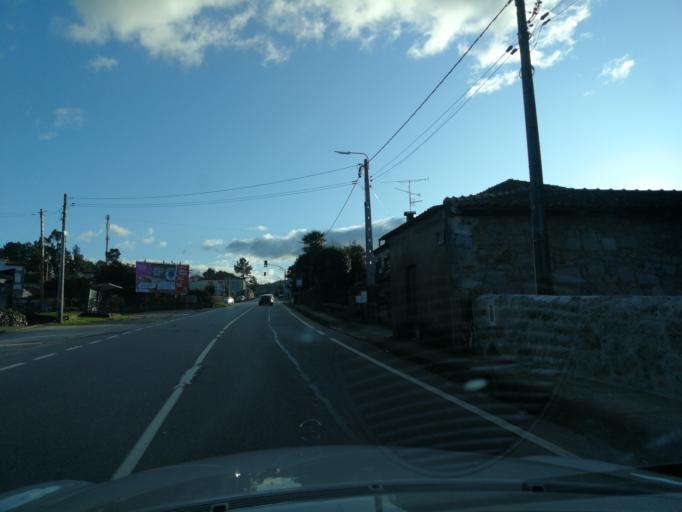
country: PT
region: Braga
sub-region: Esposende
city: Marinhas
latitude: 41.6076
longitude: -8.7405
